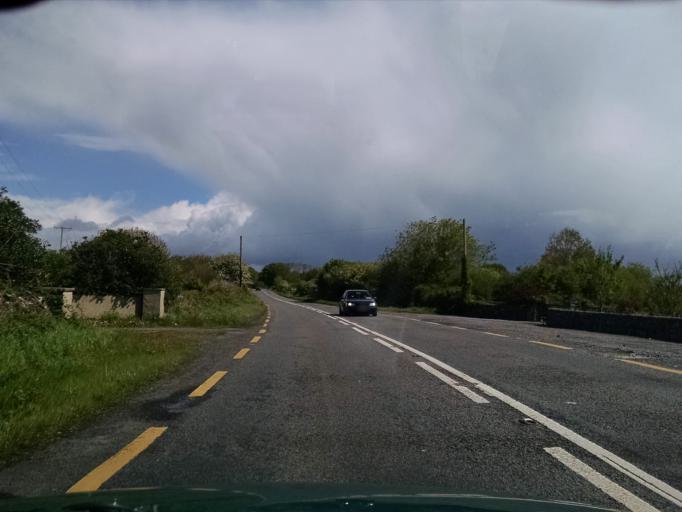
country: IE
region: Connaught
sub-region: County Galway
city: Oranmore
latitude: 53.1927
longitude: -8.8939
